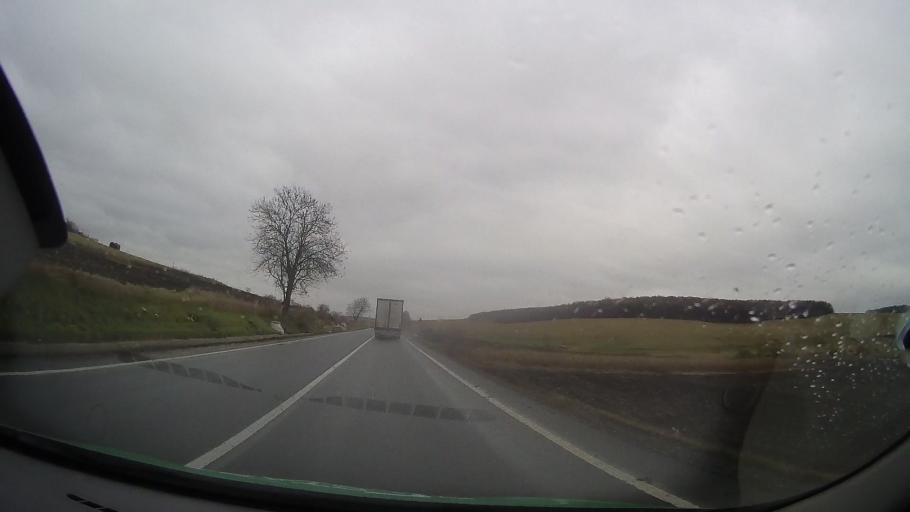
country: RO
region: Mures
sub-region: Comuna Lunca
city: Lunca
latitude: 46.8615
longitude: 24.5551
